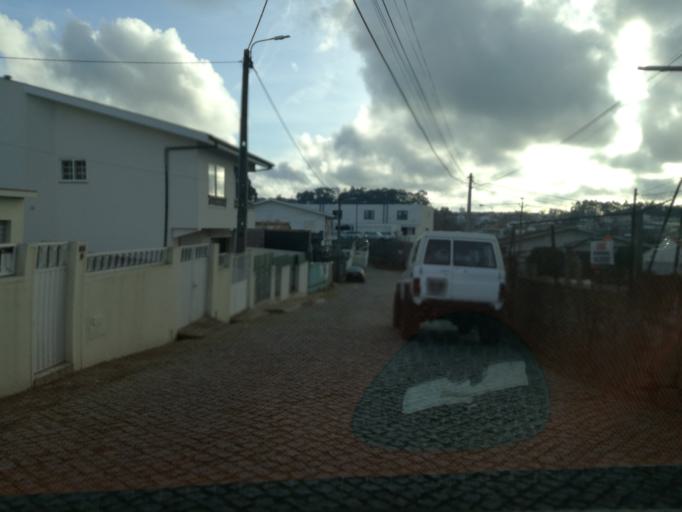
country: PT
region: Porto
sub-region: Maia
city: Nogueira
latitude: 41.2544
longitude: -8.6013
